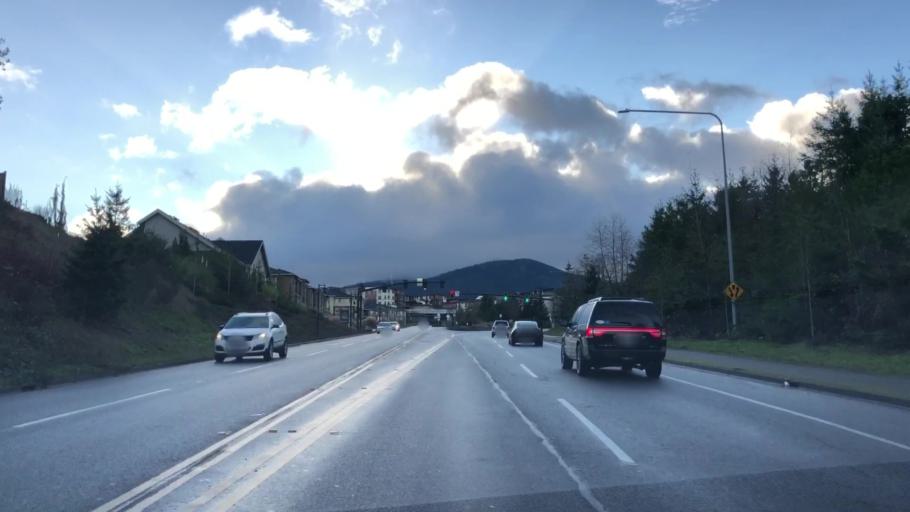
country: US
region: Washington
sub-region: King County
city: Issaquah
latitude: 47.5483
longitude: -122.0215
